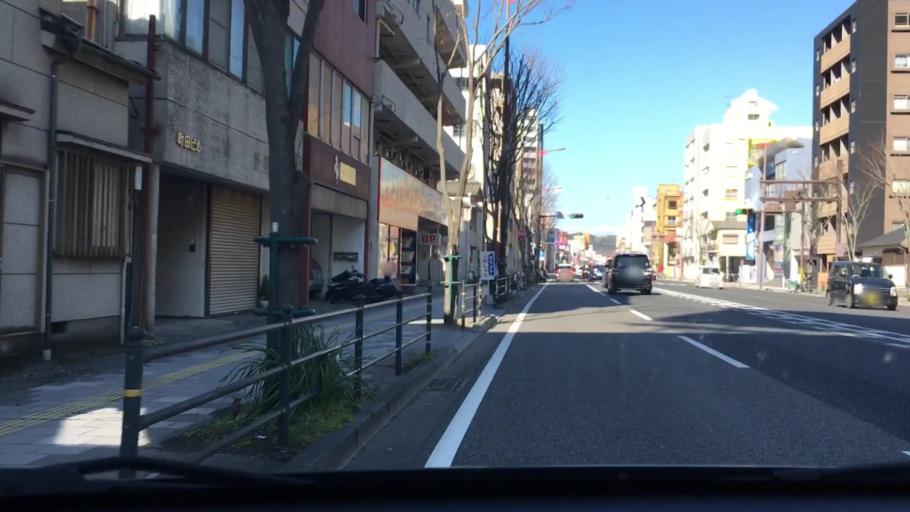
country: JP
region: Kagoshima
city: Kagoshima-shi
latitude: 31.5976
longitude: 130.5409
